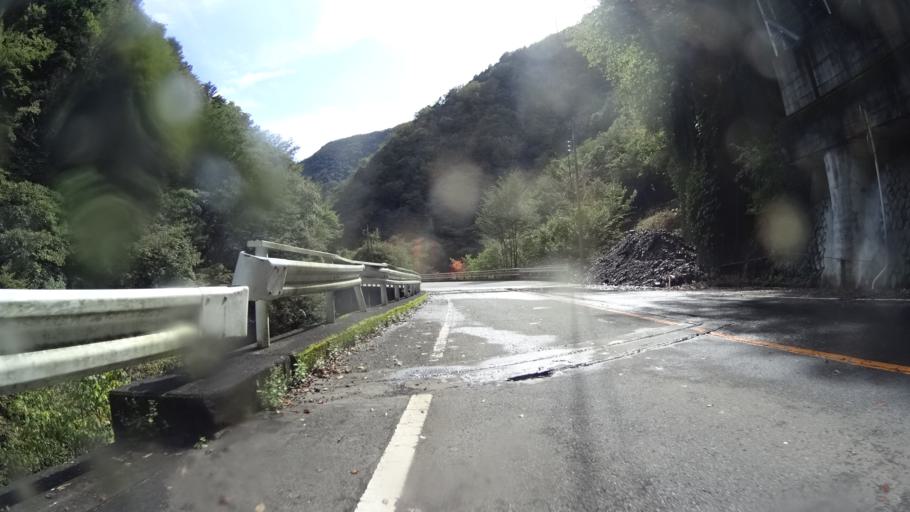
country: JP
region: Yamanashi
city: Enzan
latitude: 35.7974
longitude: 138.8958
